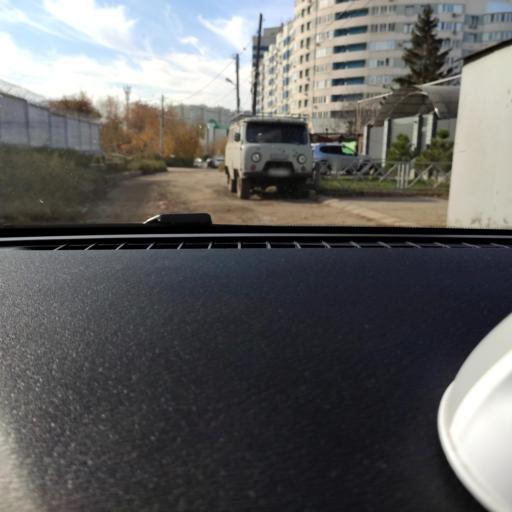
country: RU
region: Samara
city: Samara
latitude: 53.2253
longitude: 50.1771
